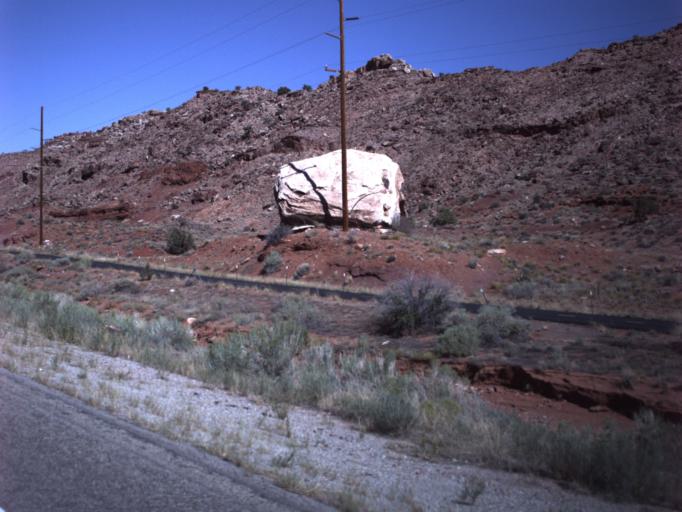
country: US
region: Utah
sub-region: Grand County
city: Moab
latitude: 38.6174
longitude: -109.6337
